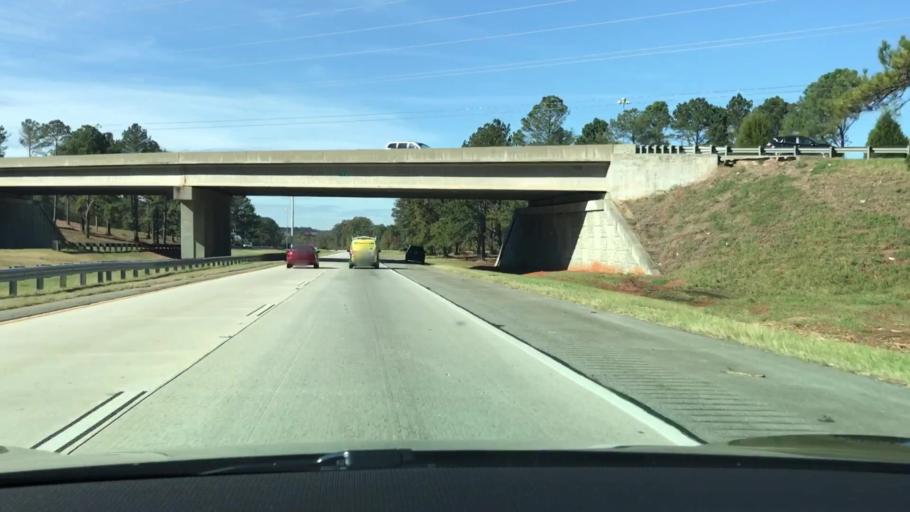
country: US
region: Georgia
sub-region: Greene County
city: Greensboro
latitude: 33.5460
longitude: -83.2046
